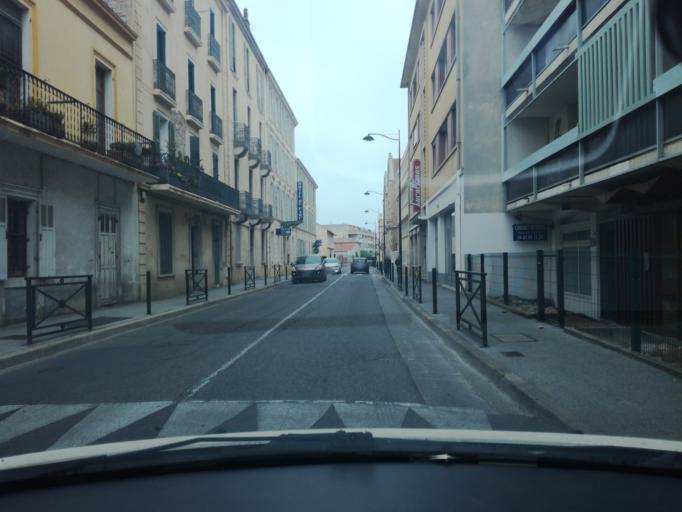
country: FR
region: Provence-Alpes-Cote d'Azur
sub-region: Departement du Var
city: Hyeres
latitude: 43.1198
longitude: 6.1332
